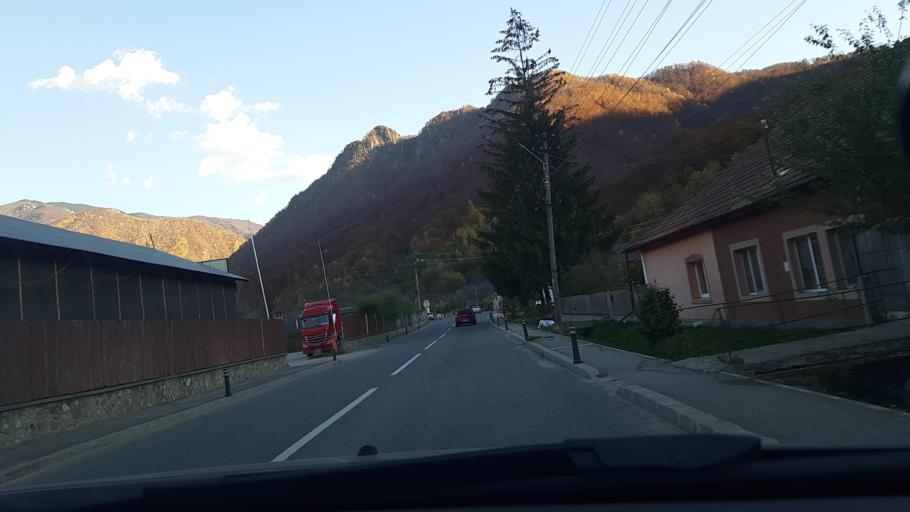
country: RO
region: Valcea
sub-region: Comuna Brezoi
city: Brezoi
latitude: 45.3352
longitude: 24.2528
